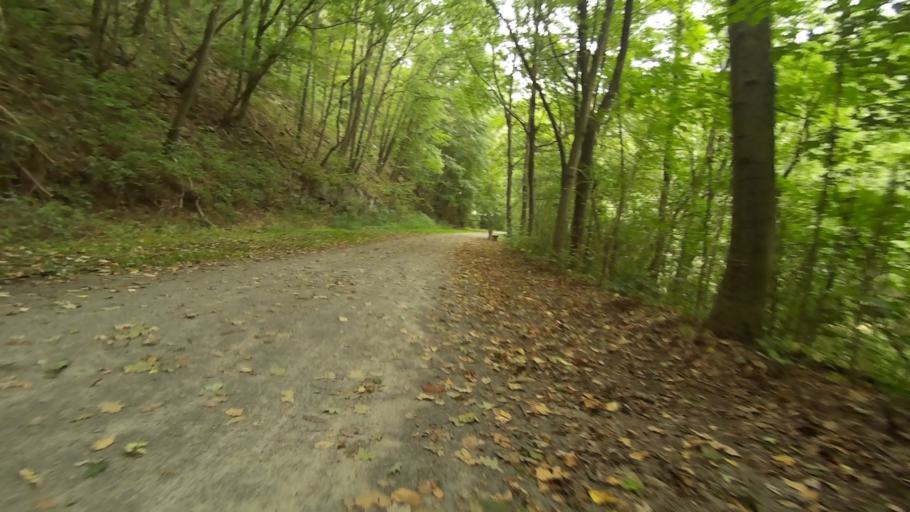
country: US
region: Pennsylvania
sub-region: Blair County
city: Williamsburg
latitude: 40.5690
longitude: -78.1366
